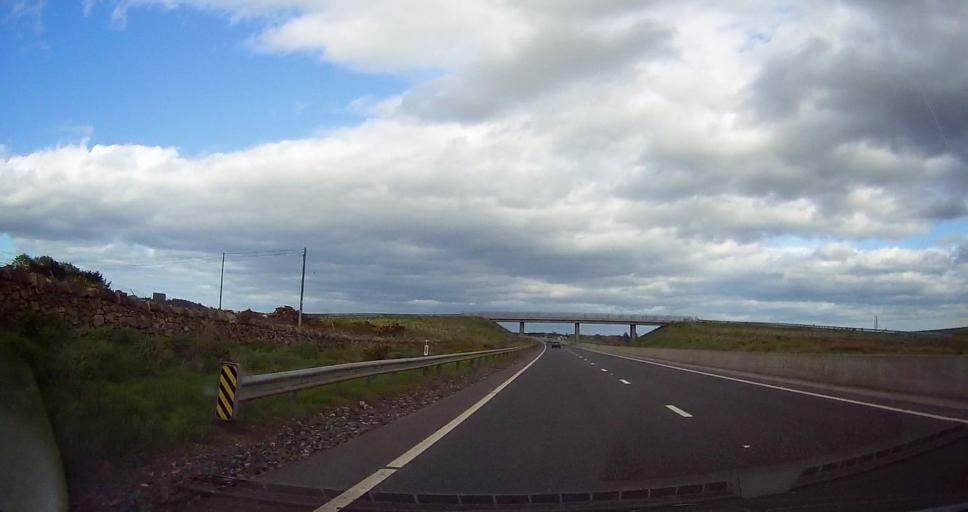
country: GB
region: Scotland
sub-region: Aberdeen City
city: Cults
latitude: 57.0809
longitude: -2.1682
